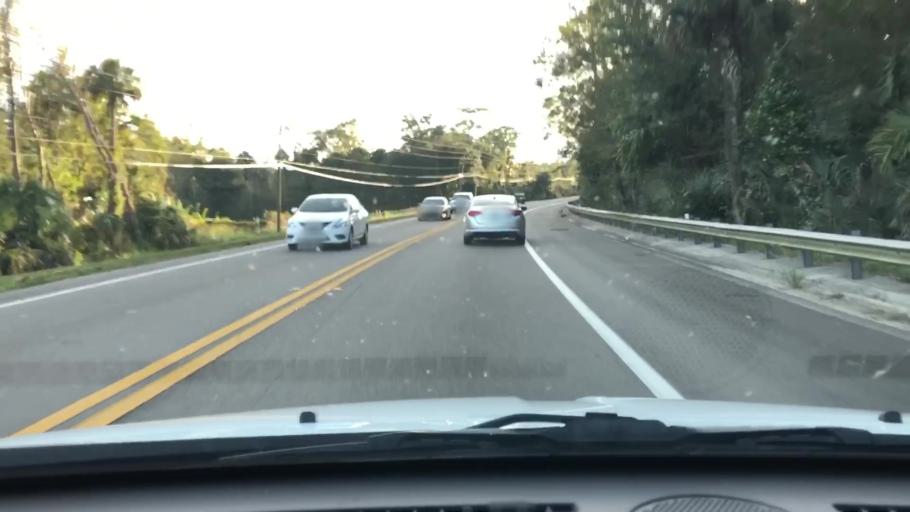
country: US
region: Florida
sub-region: Polk County
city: Loughman
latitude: 28.2652
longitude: -81.5302
